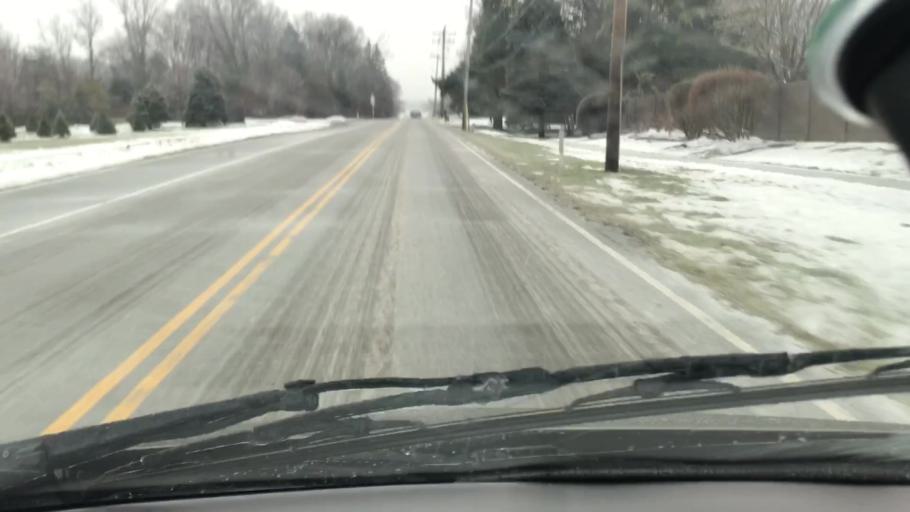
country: US
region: Indiana
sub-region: Hamilton County
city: Carmel
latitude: 39.9711
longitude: -86.0819
